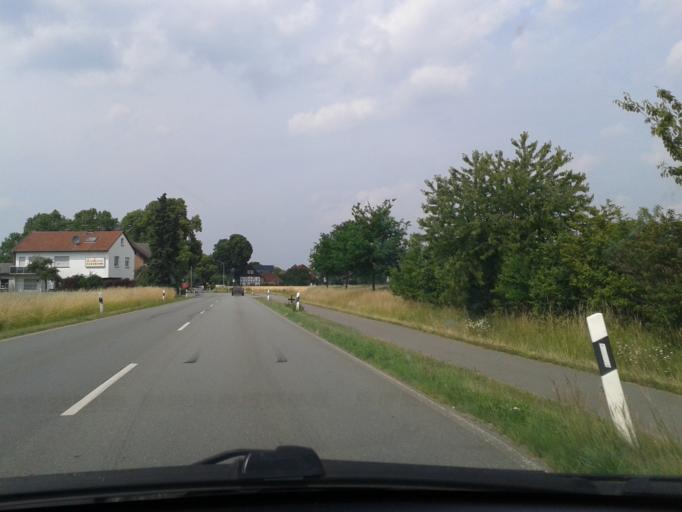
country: DE
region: North Rhine-Westphalia
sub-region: Regierungsbezirk Detmold
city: Paderborn
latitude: 51.7245
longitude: 8.6928
